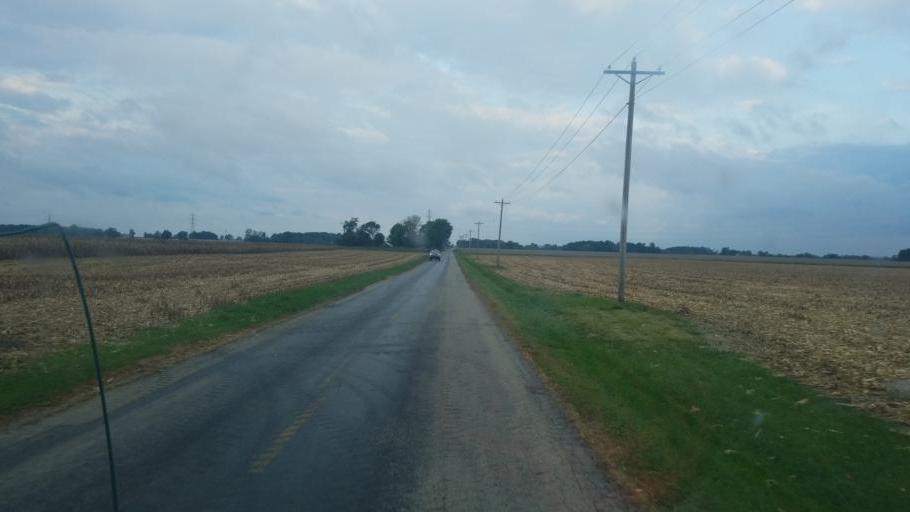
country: US
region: Ohio
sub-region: Marion County
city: Marion
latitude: 40.6738
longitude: -83.0856
